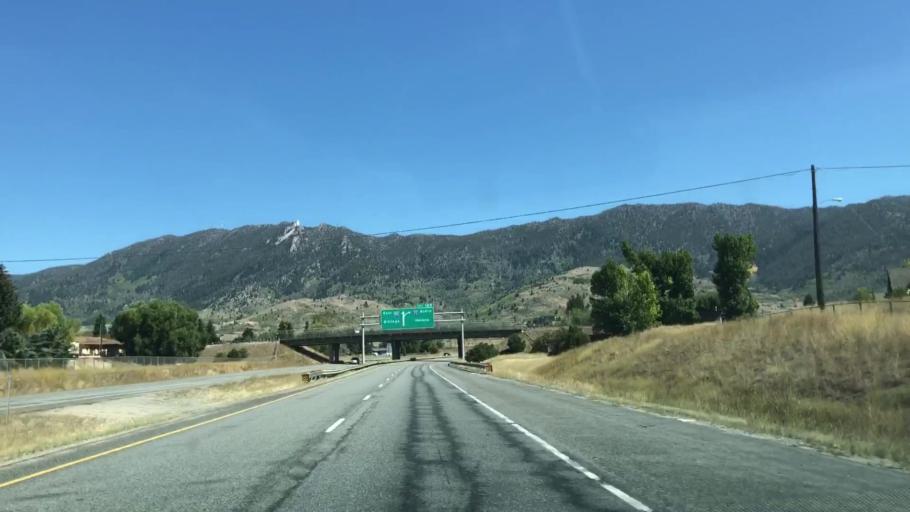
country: US
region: Montana
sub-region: Silver Bow County
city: Butte
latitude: 45.9801
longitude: -112.4950
